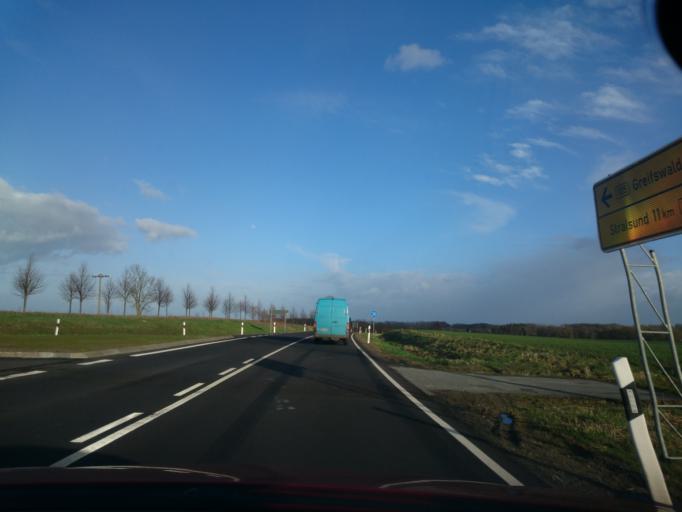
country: DE
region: Mecklenburg-Vorpommern
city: Brandshagen
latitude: 54.2356
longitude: 13.1861
